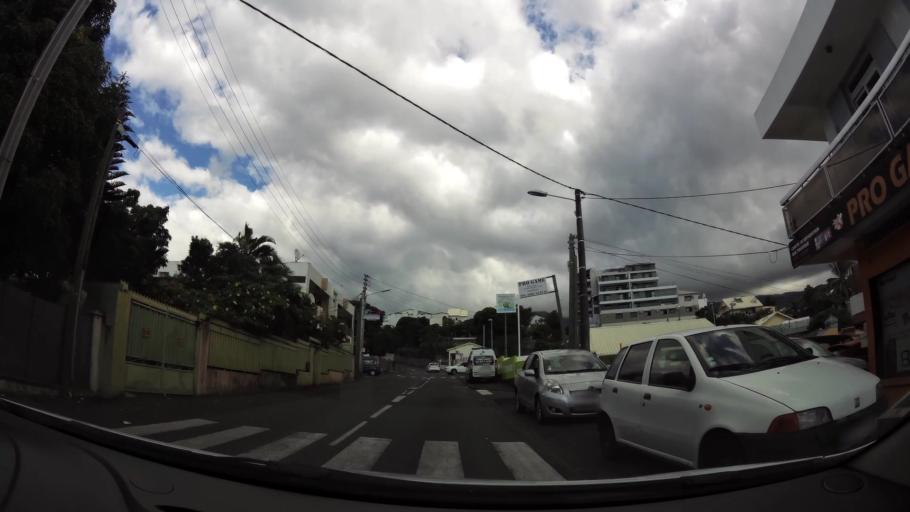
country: RE
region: Reunion
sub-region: Reunion
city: Saint-Denis
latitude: -20.8945
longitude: 55.4817
